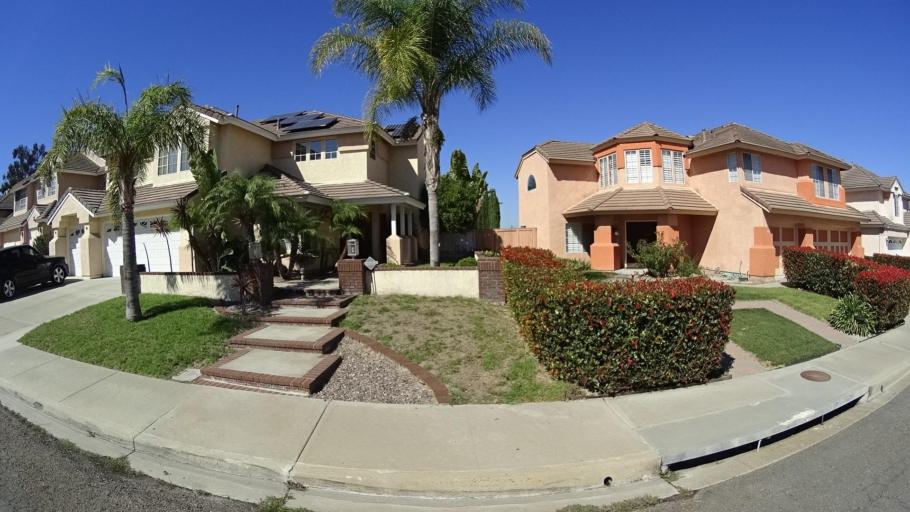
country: US
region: California
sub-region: San Diego County
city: Bonita
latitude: 32.6561
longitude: -116.9875
